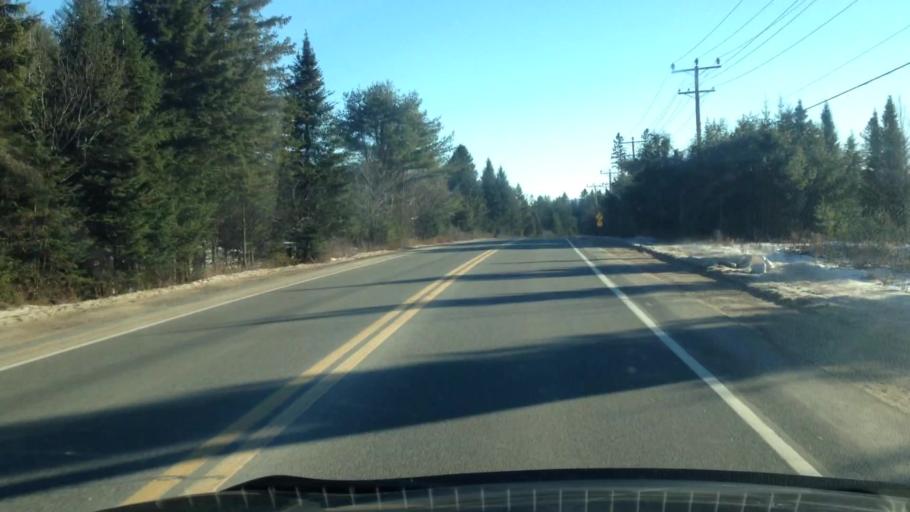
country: CA
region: Quebec
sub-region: Laurentides
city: Mont-Tremblant
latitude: 45.9946
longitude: -74.6231
